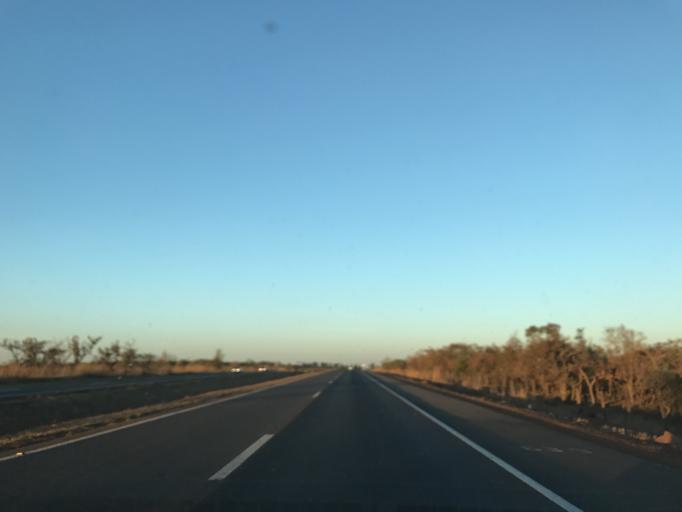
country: BR
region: Goias
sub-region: Abadiania
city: Abadiania
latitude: -16.1971
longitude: -48.7326
